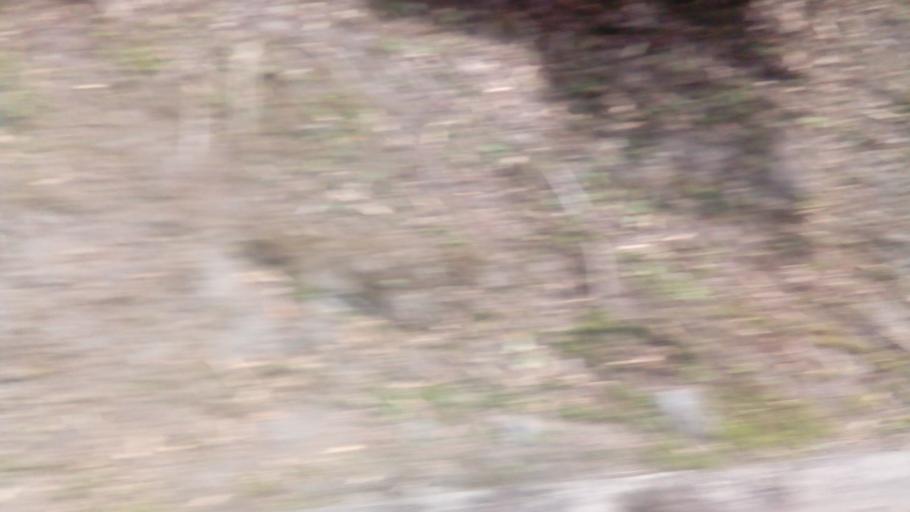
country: TW
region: Taiwan
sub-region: Yilan
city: Yilan
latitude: 24.5487
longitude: 121.4591
